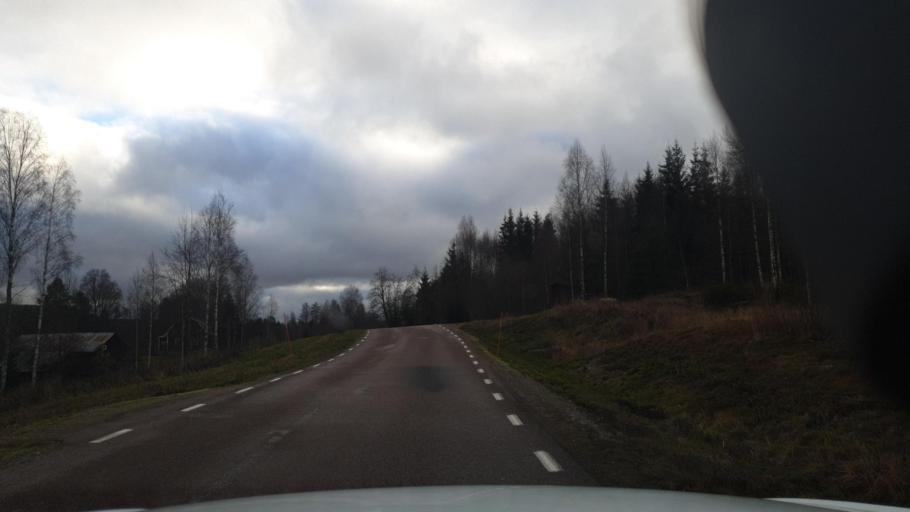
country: SE
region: Vaermland
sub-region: Arvika Kommun
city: Arvika
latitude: 59.7618
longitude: 12.8220
